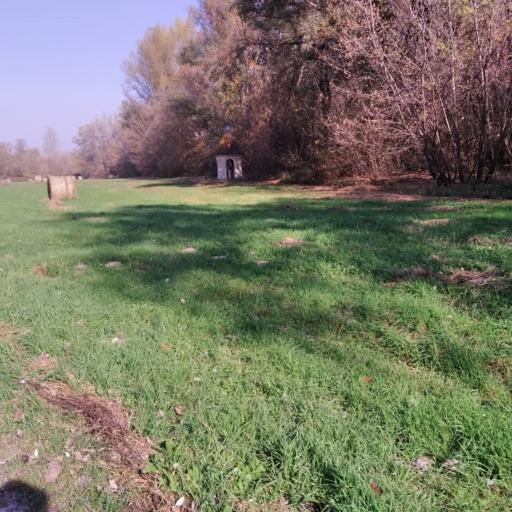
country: HU
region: Pest
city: Budakalasz
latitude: 47.5948
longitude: 19.0739
